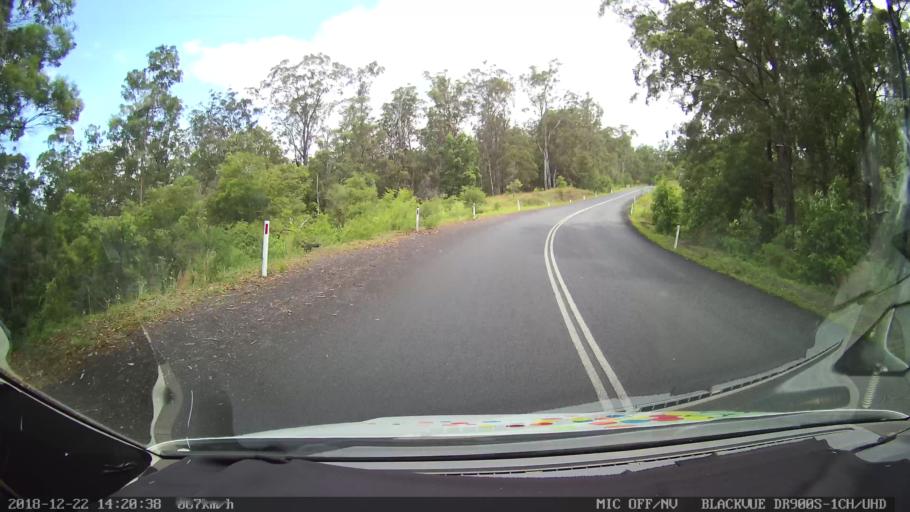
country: AU
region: New South Wales
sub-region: Clarence Valley
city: Coutts Crossing
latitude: -30.0154
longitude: 152.6642
